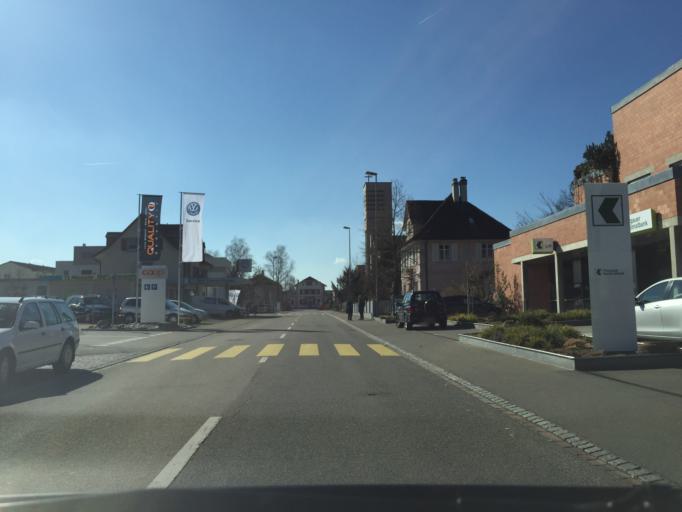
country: CH
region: Thurgau
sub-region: Frauenfeld District
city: Diessenhofen
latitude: 47.6874
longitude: 8.7536
